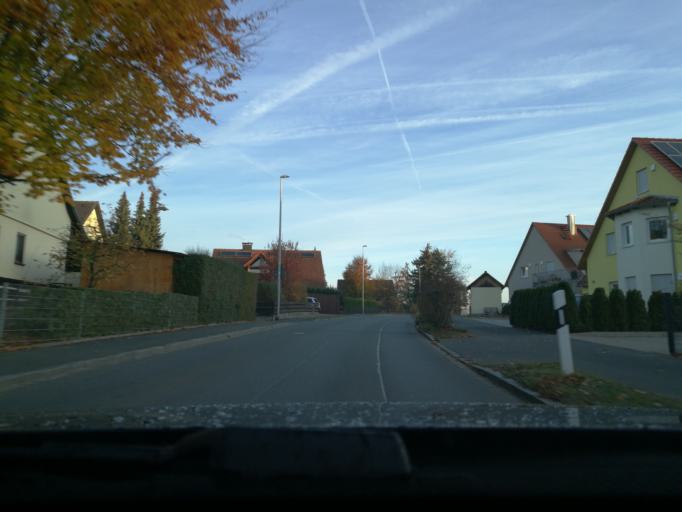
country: DE
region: Bavaria
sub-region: Regierungsbezirk Mittelfranken
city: Herzogenaurach
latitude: 49.5675
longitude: 10.9144
